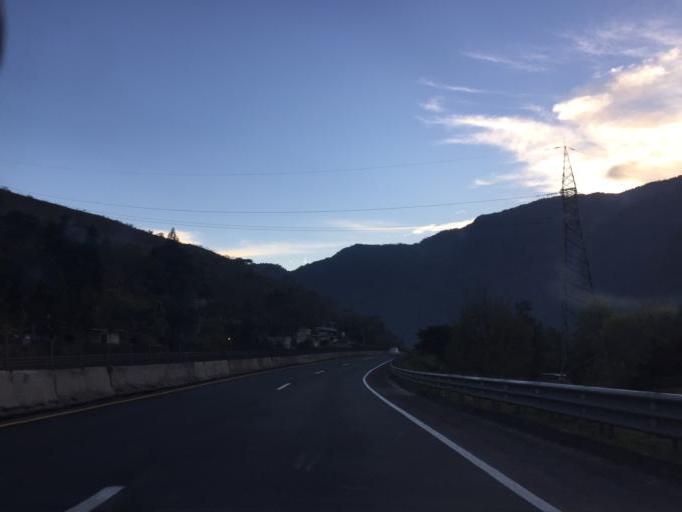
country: MX
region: Veracruz
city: Ciudad Mendoza
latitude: 18.8180
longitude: -97.1705
